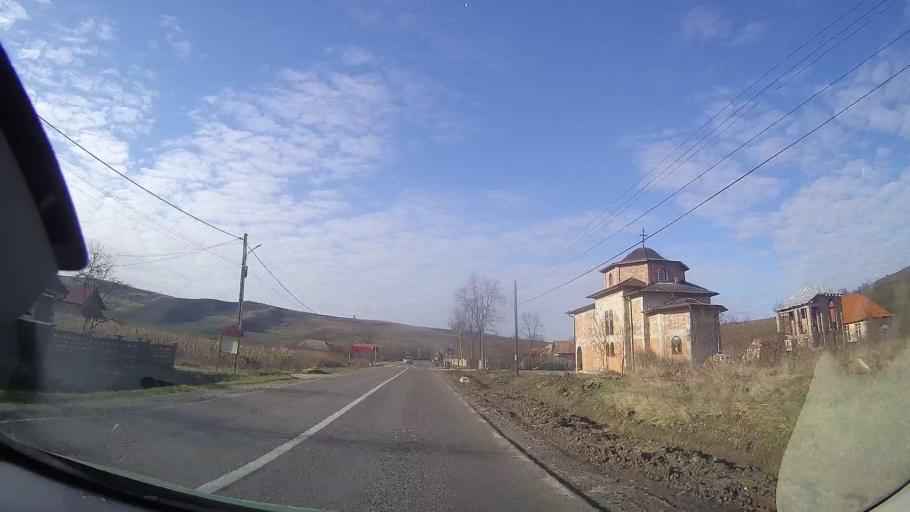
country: RO
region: Cluj
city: Caianu Mic
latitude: 46.7984
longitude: 23.8782
